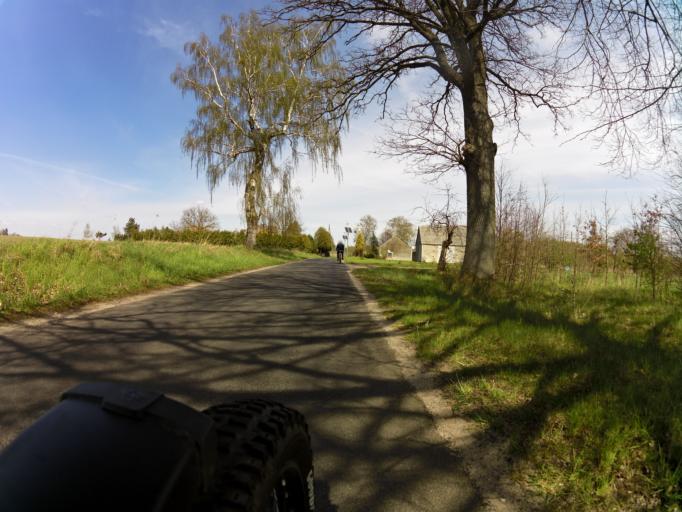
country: PL
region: West Pomeranian Voivodeship
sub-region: Powiat lobeski
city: Resko
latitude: 53.7895
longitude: 15.4273
